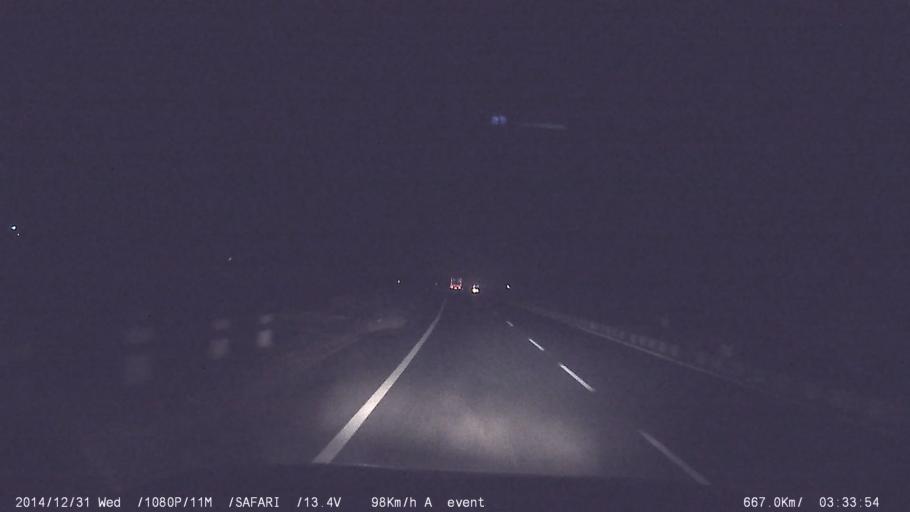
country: IN
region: Tamil Nadu
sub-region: Salem
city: Belur
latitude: 11.6543
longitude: 78.4413
